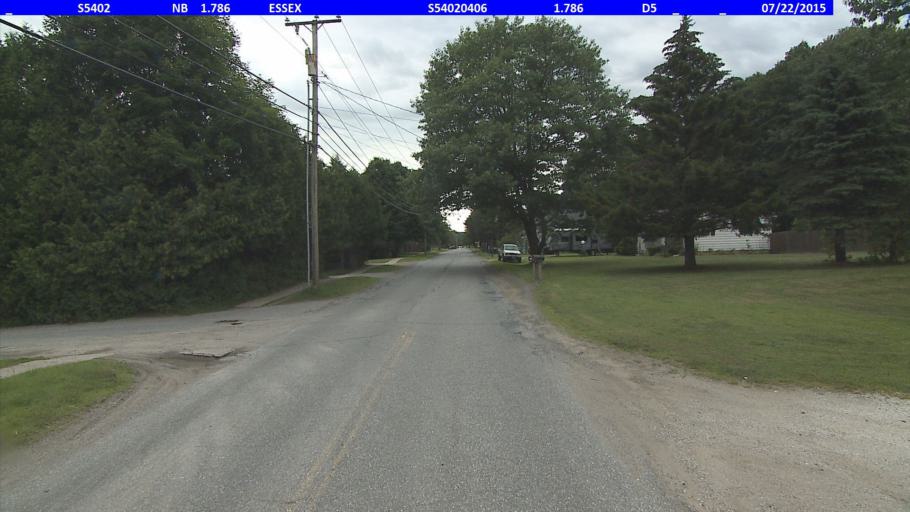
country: US
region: Vermont
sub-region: Chittenden County
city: Jericho
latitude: 44.5035
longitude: -73.0512
